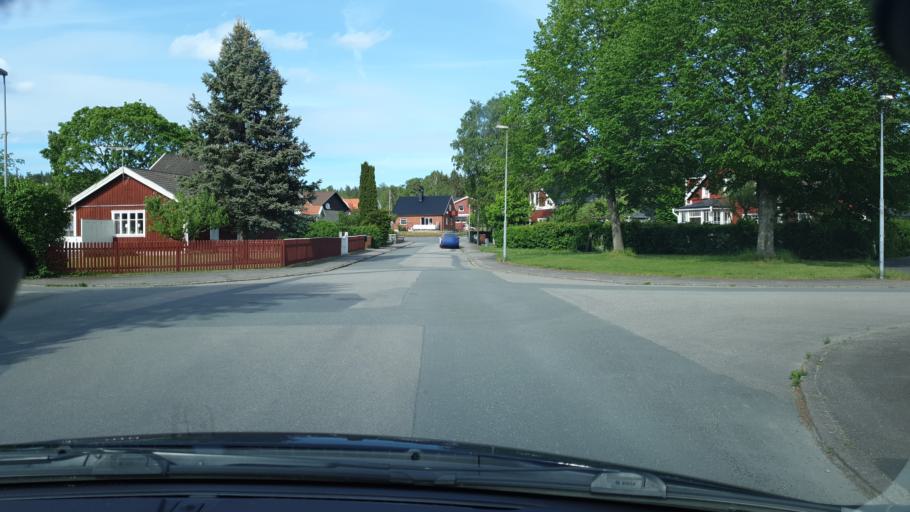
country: SE
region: Joenkoeping
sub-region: Vetlanda Kommun
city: Vetlanda
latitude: 57.4316
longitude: 15.0910
